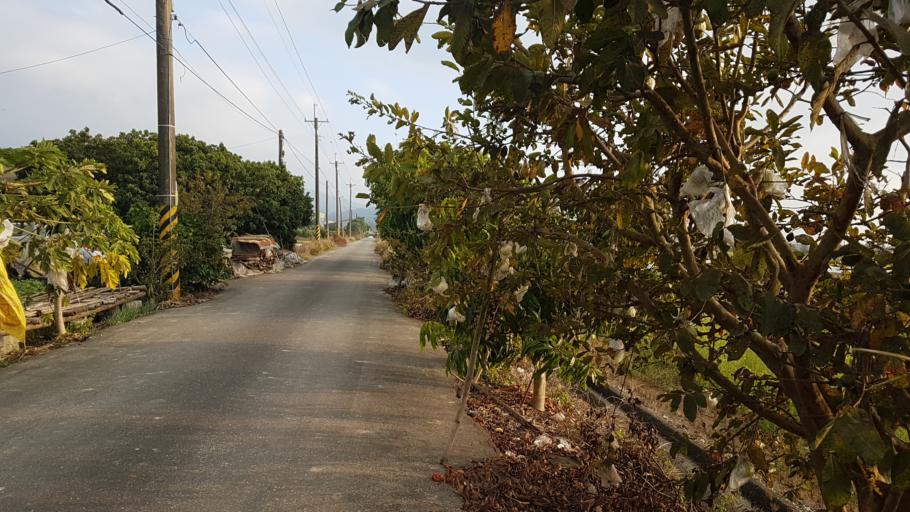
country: TW
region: Taiwan
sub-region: Chiayi
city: Jiayi Shi
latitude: 23.3743
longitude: 120.4538
